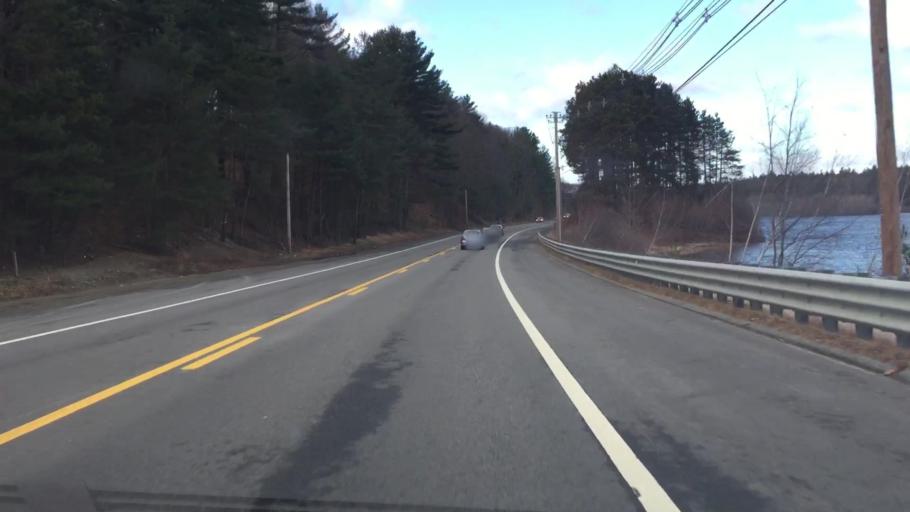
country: US
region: Massachusetts
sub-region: Worcester County
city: West Boylston
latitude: 42.3402
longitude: -71.7554
